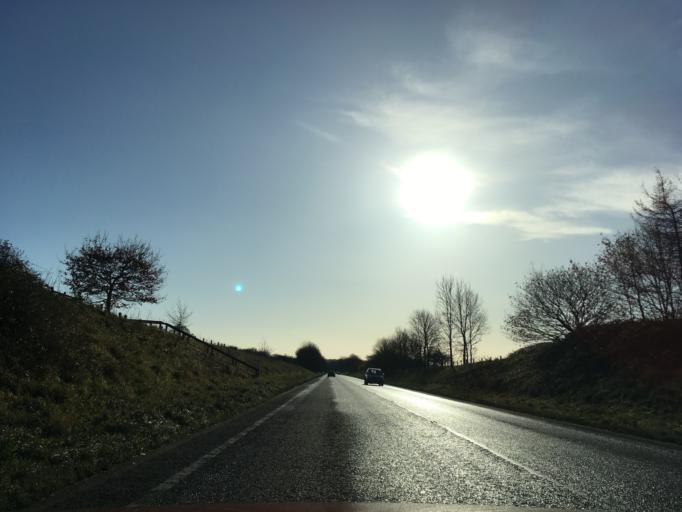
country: GB
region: England
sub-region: Wiltshire
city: Burbage
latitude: 51.3519
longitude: -1.6759
